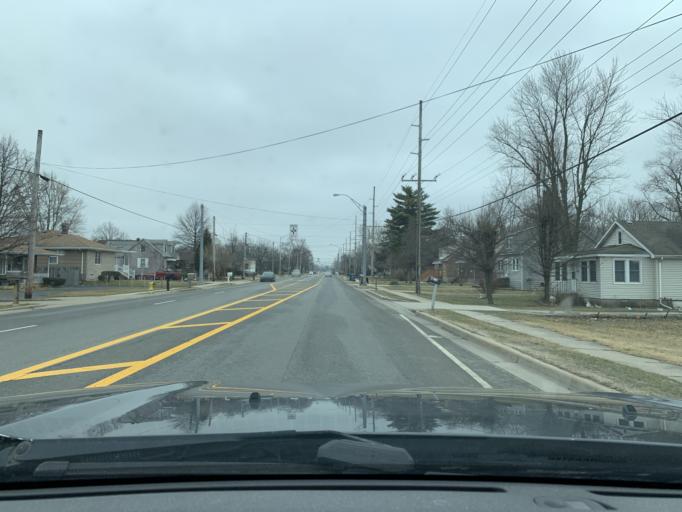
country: US
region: Indiana
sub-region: Lake County
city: Highland
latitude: 41.5353
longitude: -87.4616
